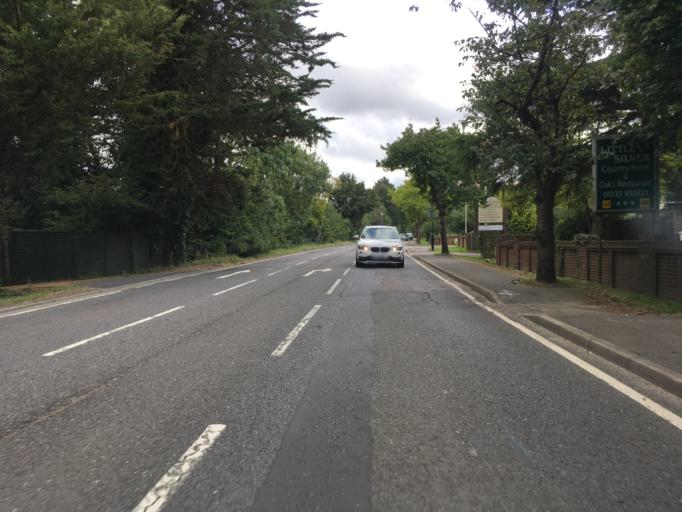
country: GB
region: England
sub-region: Kent
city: Tenterden
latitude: 51.0909
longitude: 0.6903
